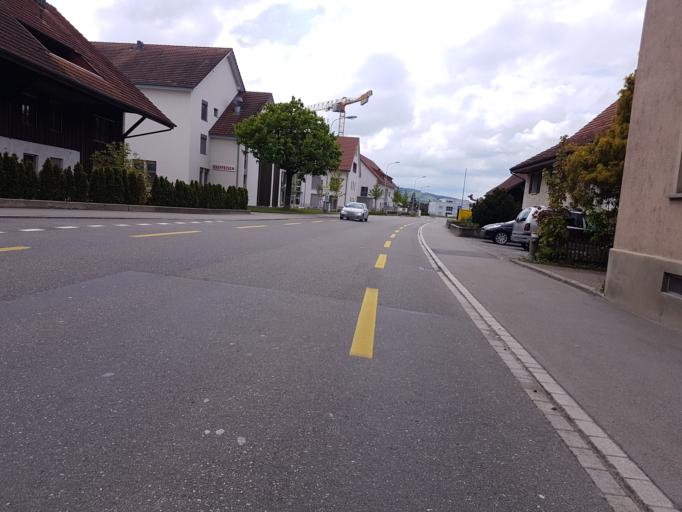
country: CH
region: Aargau
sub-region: Bezirk Baden
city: Wurenlingen
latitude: 47.5336
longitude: 8.2543
